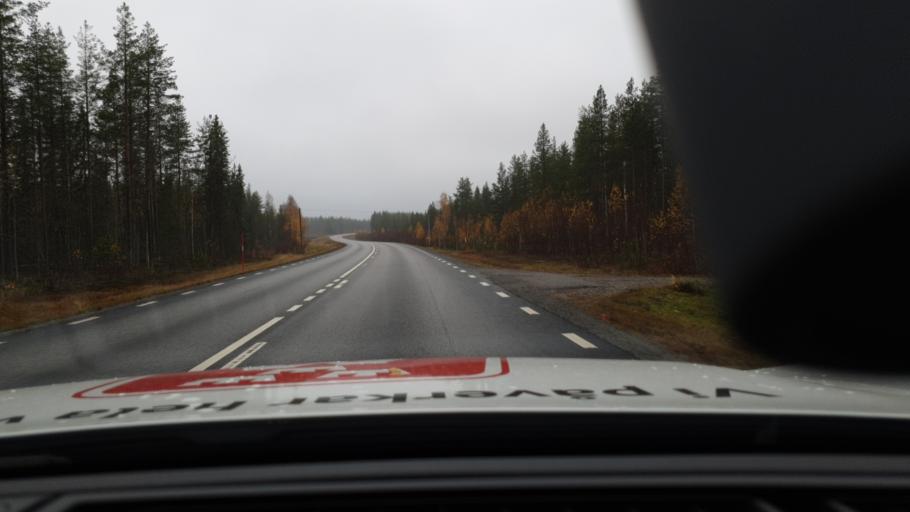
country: SE
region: Norrbotten
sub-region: Overkalix Kommun
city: OEverkalix
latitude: 66.6062
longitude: 22.2519
